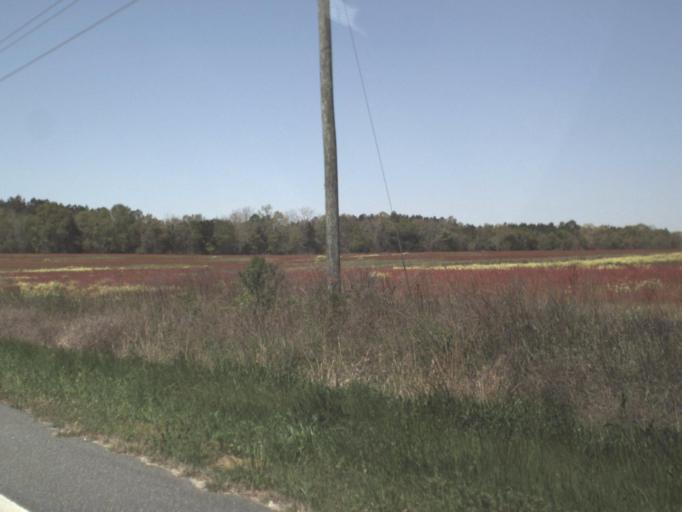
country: US
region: Florida
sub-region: Jackson County
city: Graceville
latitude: 30.9727
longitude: -85.6278
